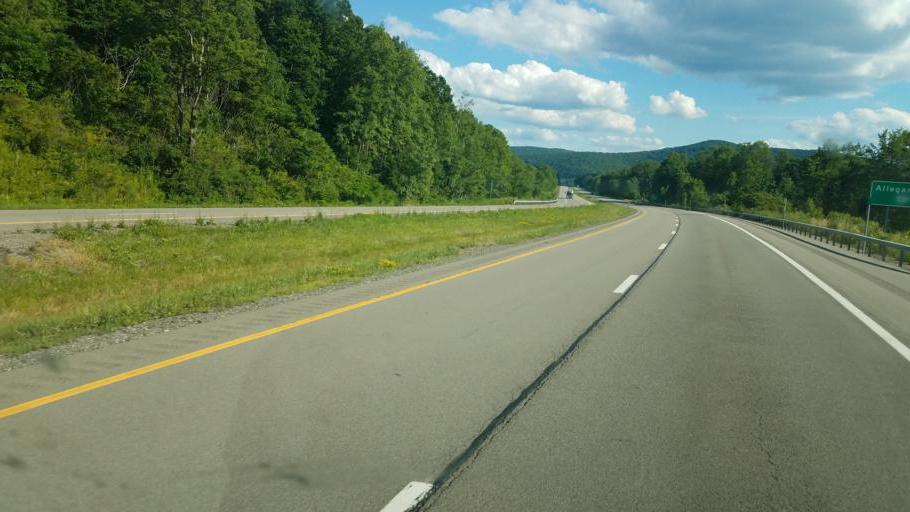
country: US
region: New York
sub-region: Cattaraugus County
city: Salamanca
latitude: 42.1315
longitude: -78.7797
